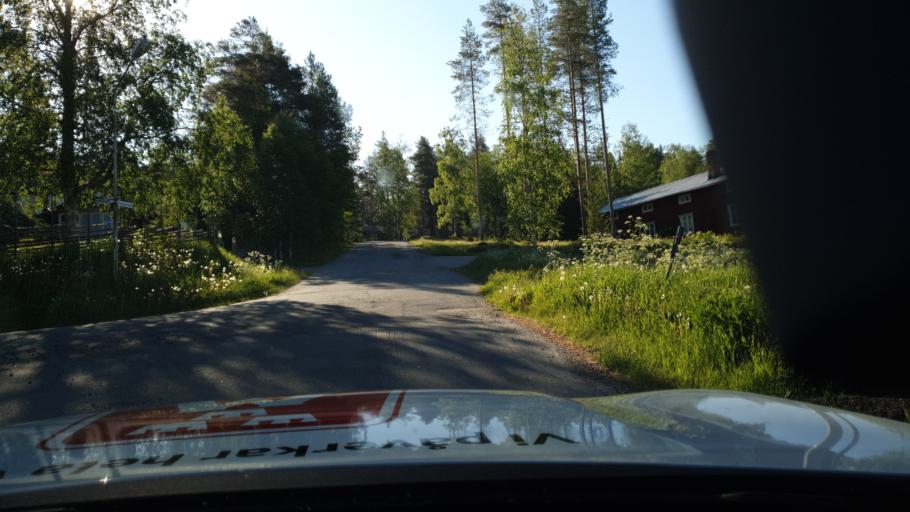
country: SE
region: Vaesterbotten
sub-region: Vindelns Kommun
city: Vindeln
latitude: 64.1891
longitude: 19.7093
